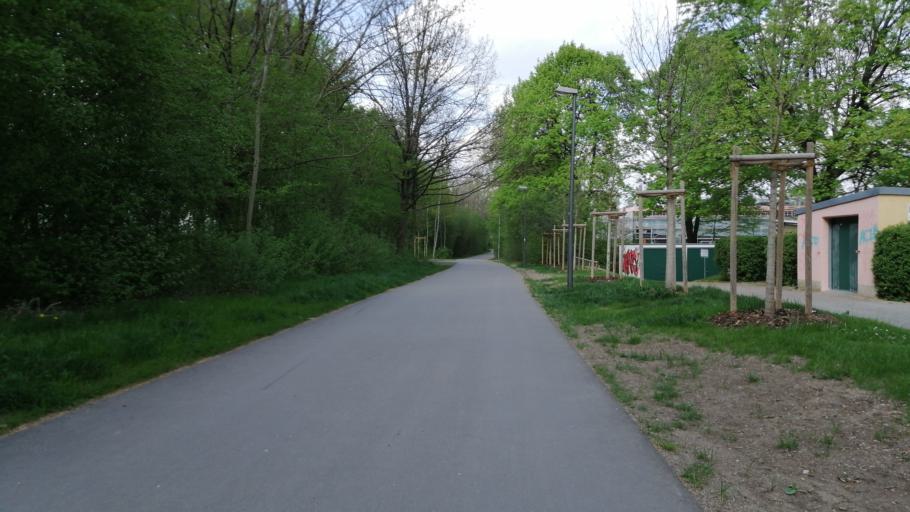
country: DE
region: Bavaria
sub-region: Upper Bavaria
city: Bogenhausen
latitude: 48.1620
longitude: 11.6374
